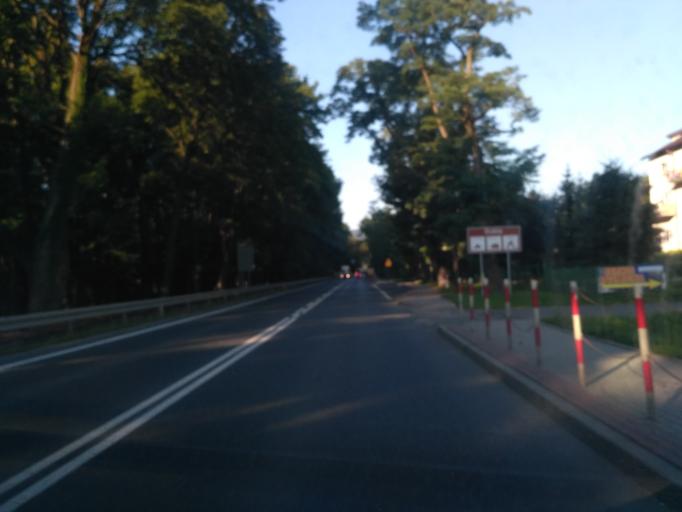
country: PL
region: Subcarpathian Voivodeship
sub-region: Powiat krosnienski
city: Dukla
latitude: 49.5610
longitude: 21.6880
